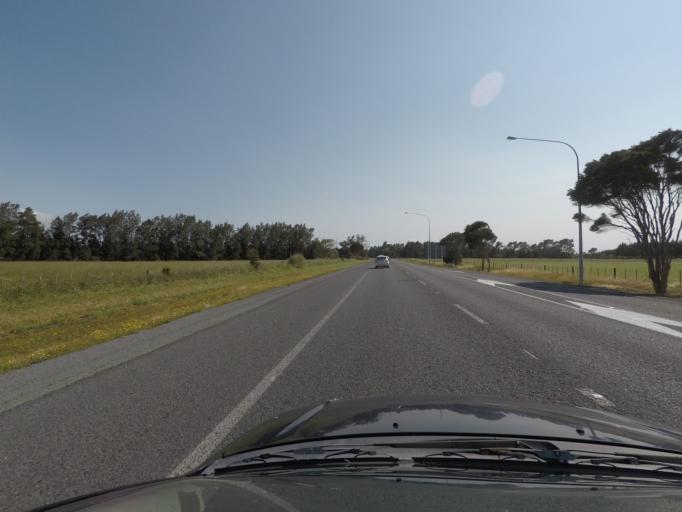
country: NZ
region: Northland
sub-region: Whangarei
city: Ruakaka
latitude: -35.9630
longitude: 174.4468
